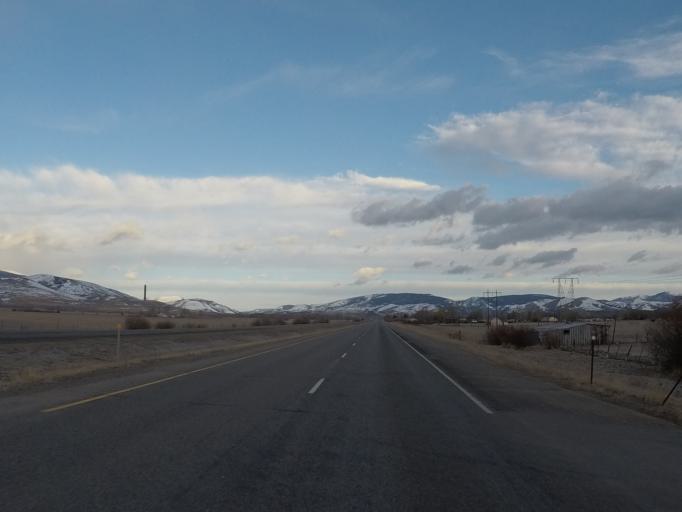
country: US
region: Montana
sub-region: Deer Lodge County
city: Warm Springs
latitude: 46.0975
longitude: -112.8282
